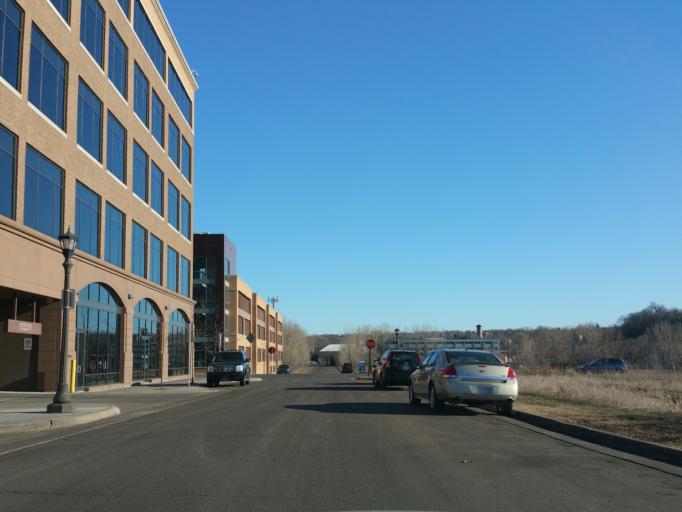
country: US
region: Minnesota
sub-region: Ramsey County
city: Saint Paul
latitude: 44.9416
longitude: -93.0867
